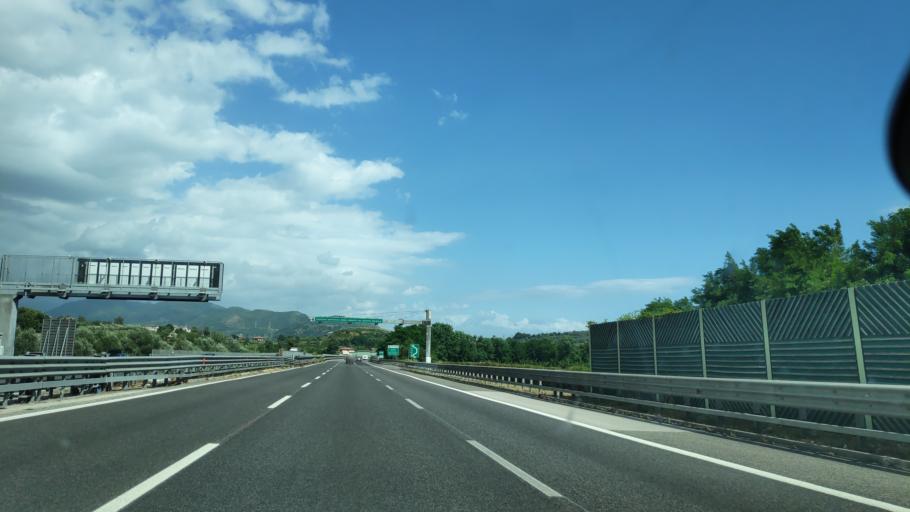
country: IT
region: Campania
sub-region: Provincia di Salerno
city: San Mango Piemonte
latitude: 40.6869
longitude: 14.8465
